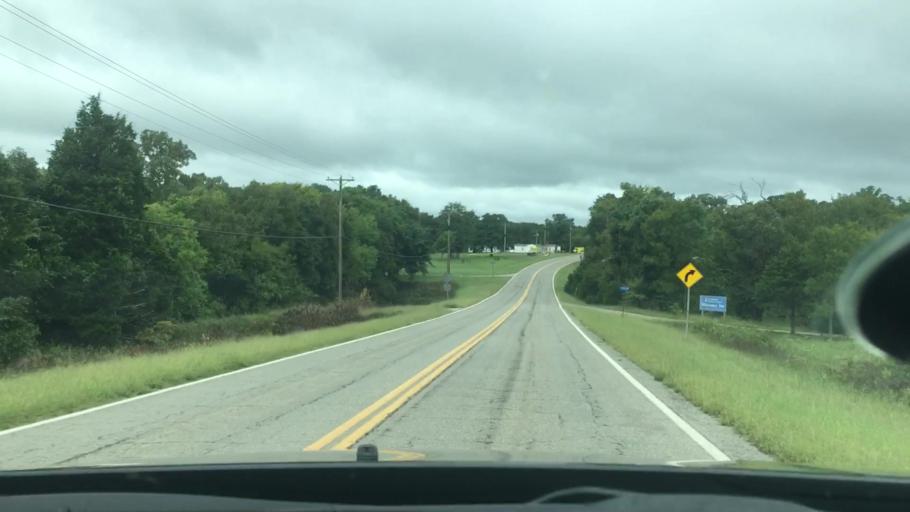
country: US
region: Oklahoma
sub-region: Cherokee County
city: Park Hill
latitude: 35.6922
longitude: -94.9129
